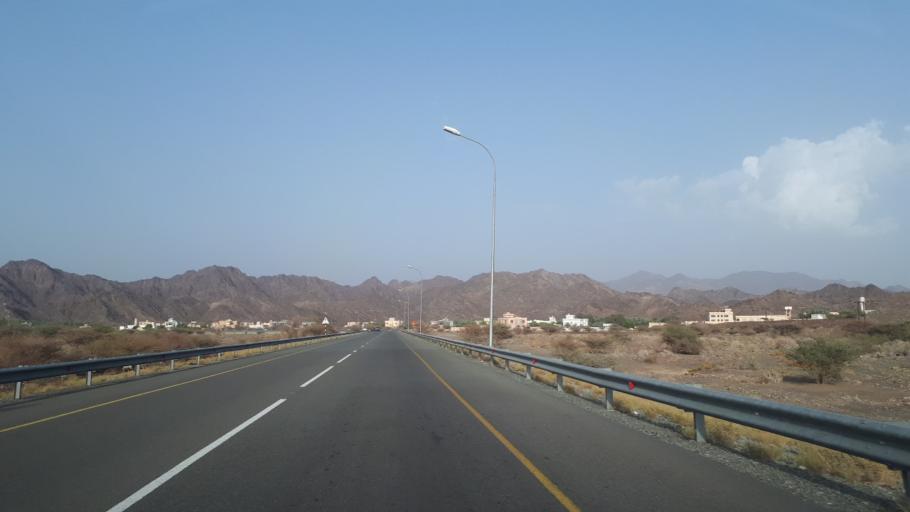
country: OM
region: Az Zahirah
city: Yanqul
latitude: 23.4863
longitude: 56.8185
